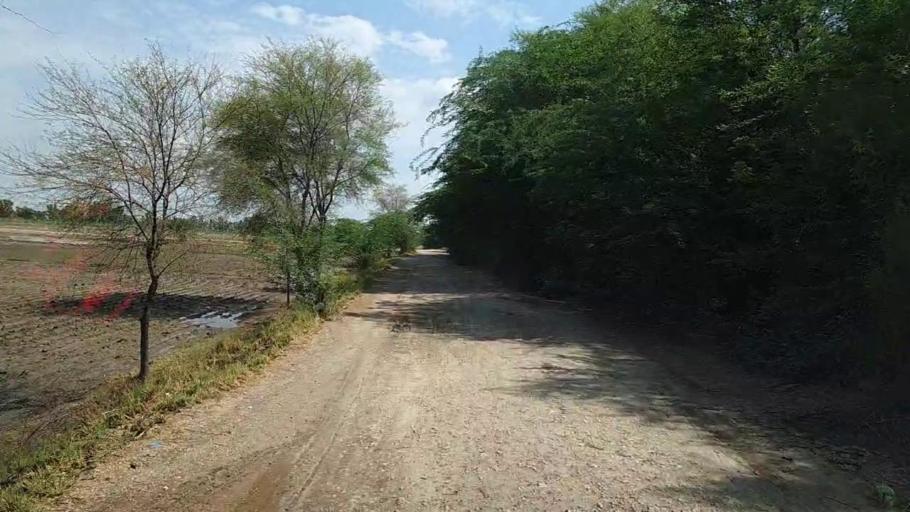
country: PK
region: Sindh
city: Bhiria
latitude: 26.9207
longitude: 68.2266
